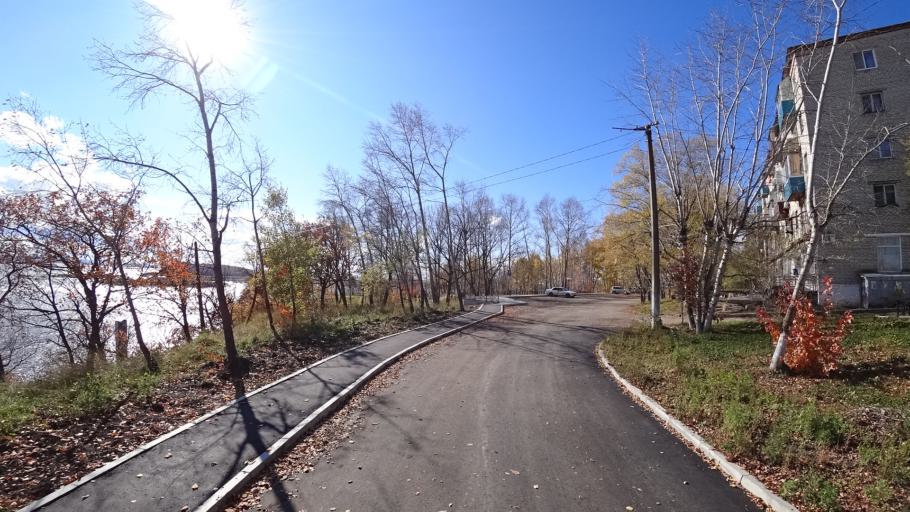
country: RU
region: Khabarovsk Krai
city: Amursk
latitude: 50.2150
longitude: 136.9057
